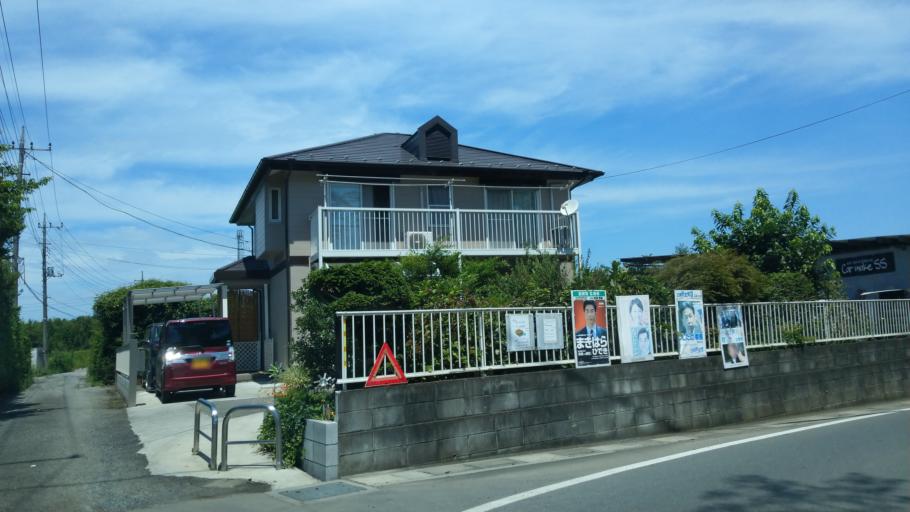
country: JP
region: Saitama
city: Ageoshimo
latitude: 35.9309
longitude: 139.5640
